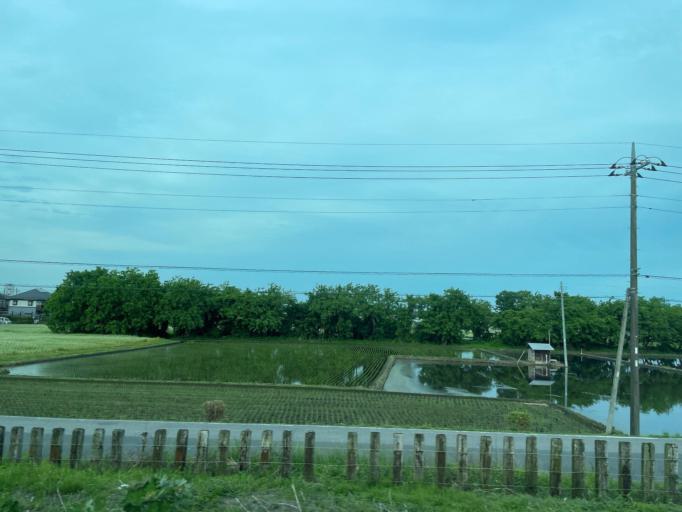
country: JP
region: Tochigi
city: Kanuma
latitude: 36.5317
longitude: 139.7420
